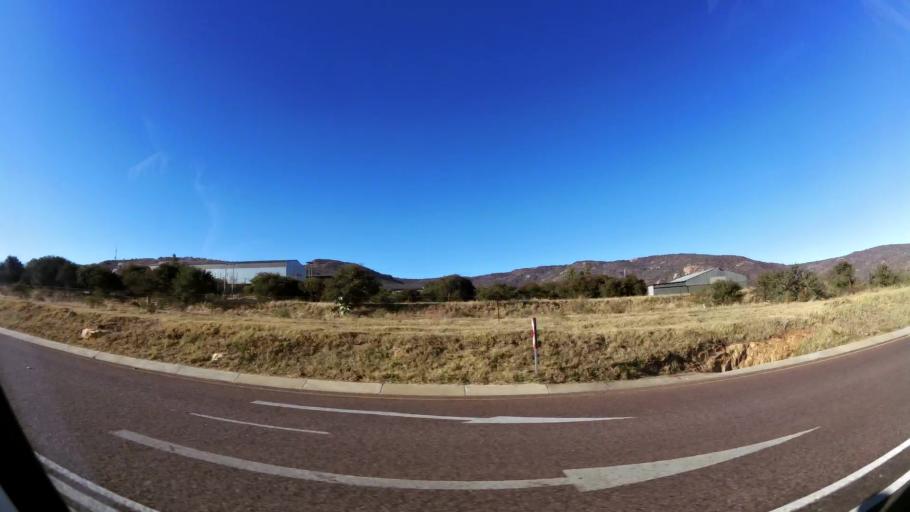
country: ZA
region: Limpopo
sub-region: Capricorn District Municipality
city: Mankoeng
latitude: -23.9296
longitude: 29.8574
